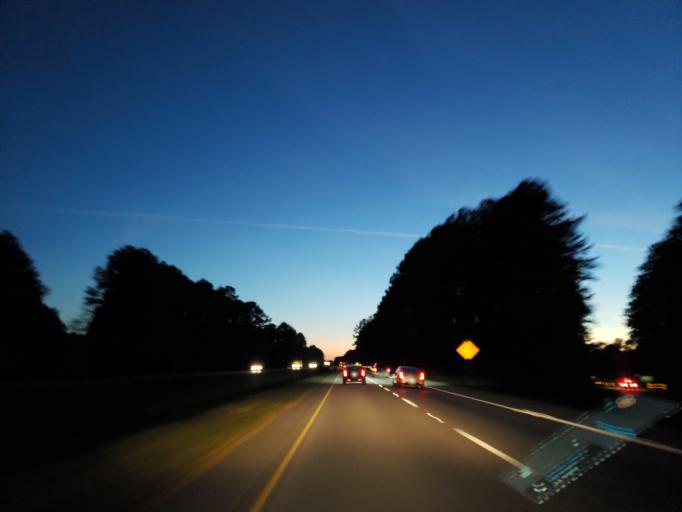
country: US
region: Mississippi
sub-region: Clarke County
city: Stonewall
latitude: 32.2074
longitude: -88.8422
